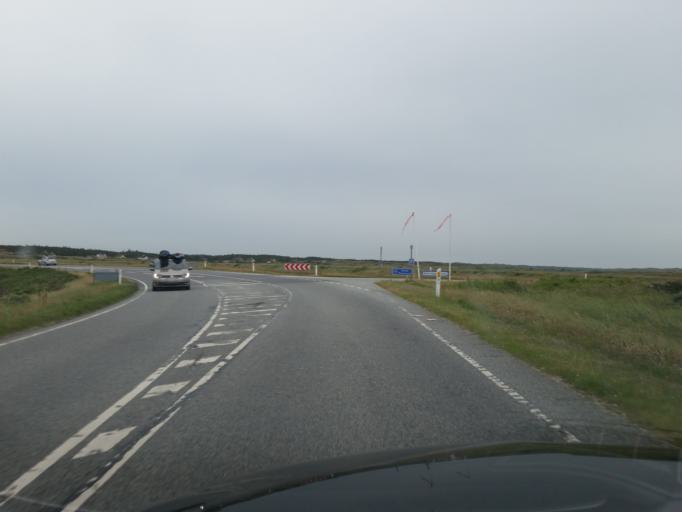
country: DK
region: Central Jutland
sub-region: Ringkobing-Skjern Kommune
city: Hvide Sande
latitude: 55.8194
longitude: 8.1822
